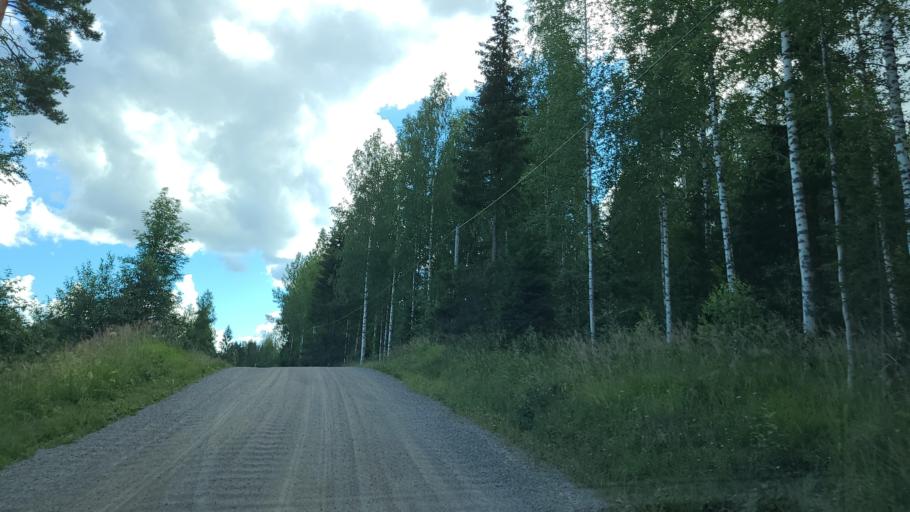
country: FI
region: Central Finland
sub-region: Jaemsae
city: Jaemsae
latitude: 61.9175
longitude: 25.3060
